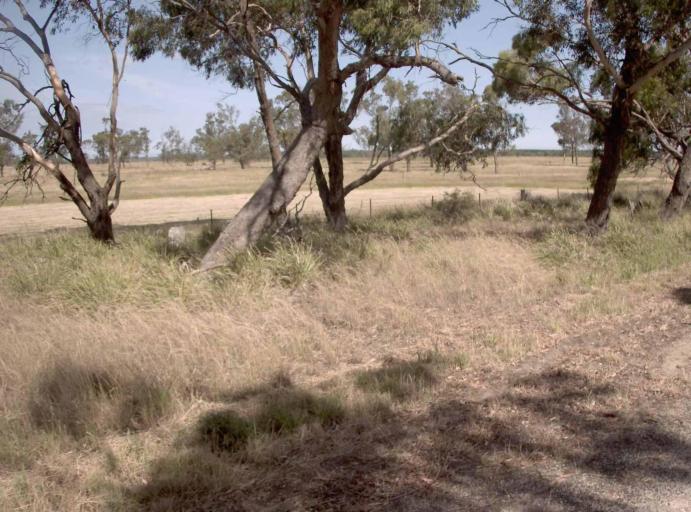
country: AU
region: Victoria
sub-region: Wellington
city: Sale
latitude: -38.2810
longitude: 147.1524
